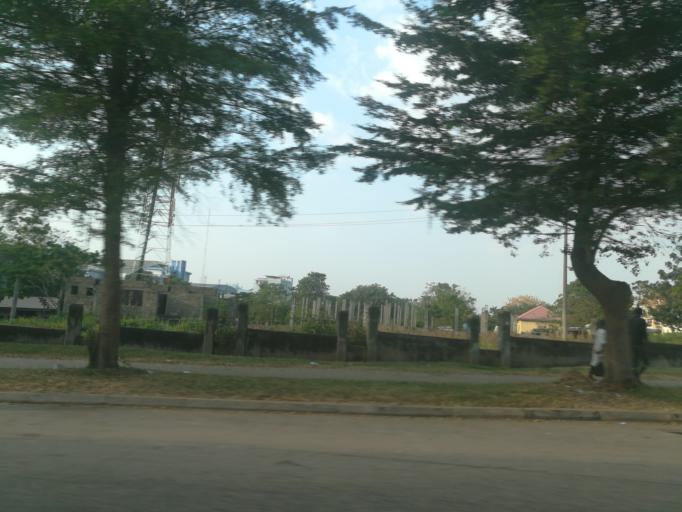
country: NG
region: Abuja Federal Capital Territory
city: Abuja
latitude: 9.0669
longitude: 7.4366
